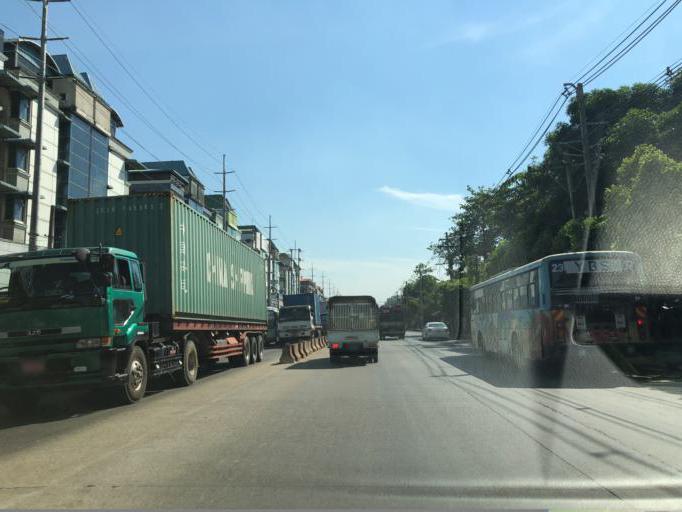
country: MM
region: Yangon
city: Yangon
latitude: 16.8311
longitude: 96.1214
